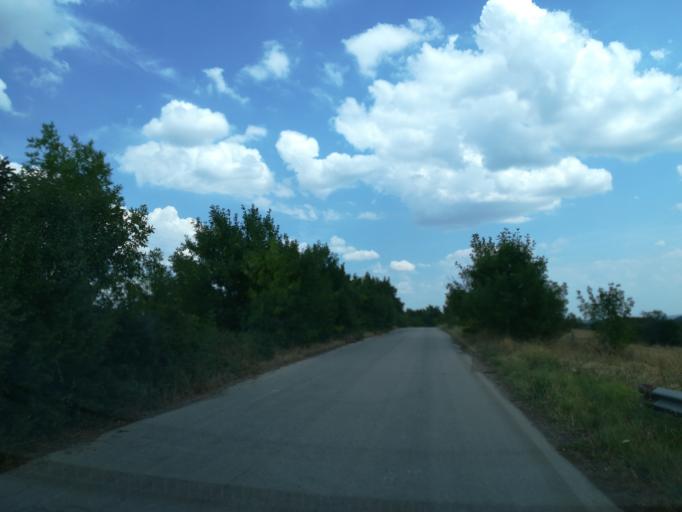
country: BG
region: Khaskovo
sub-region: Obshtina Mineralni Bani
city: Mineralni Bani
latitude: 41.9782
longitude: 25.1551
